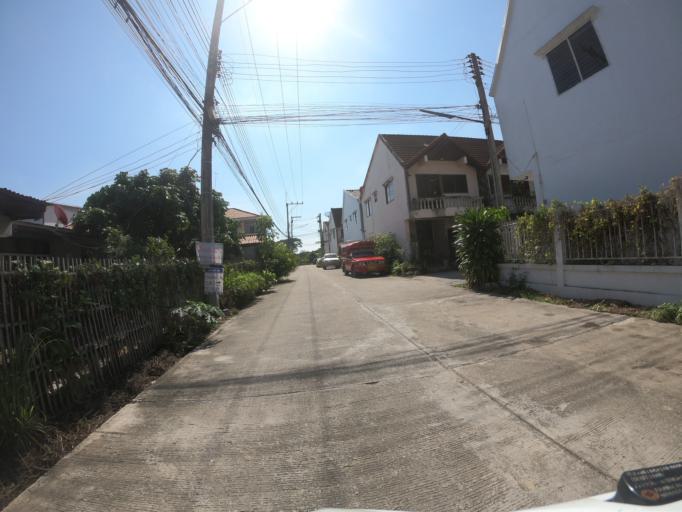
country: TH
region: Chiang Mai
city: Chiang Mai
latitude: 18.7479
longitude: 98.9648
